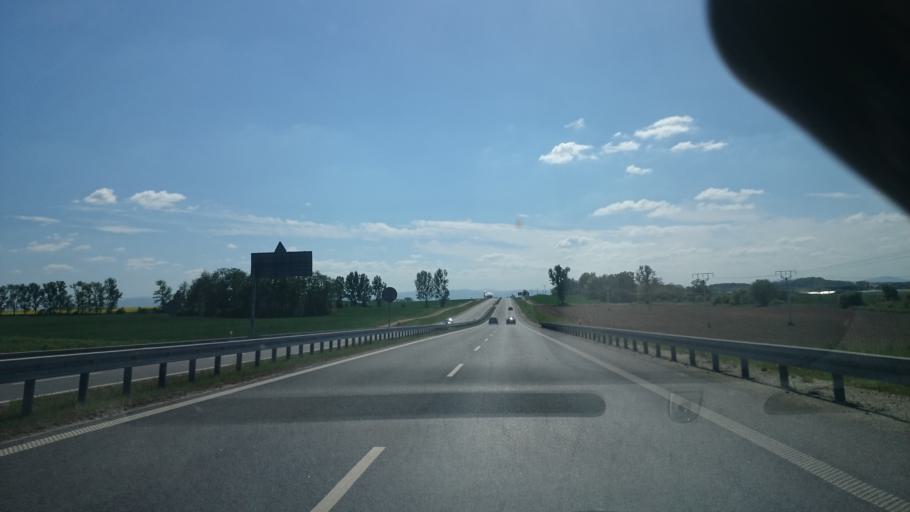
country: PL
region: Opole Voivodeship
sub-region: Powiat nyski
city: Nysa
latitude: 50.4954
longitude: 17.2869
